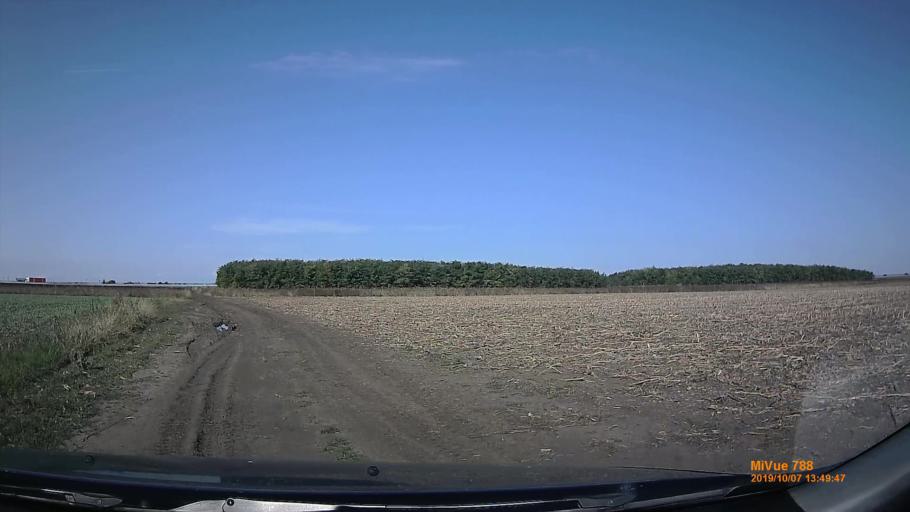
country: HU
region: Jasz-Nagykun-Szolnok
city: Cserkeszolo
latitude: 46.8811
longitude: 20.2181
